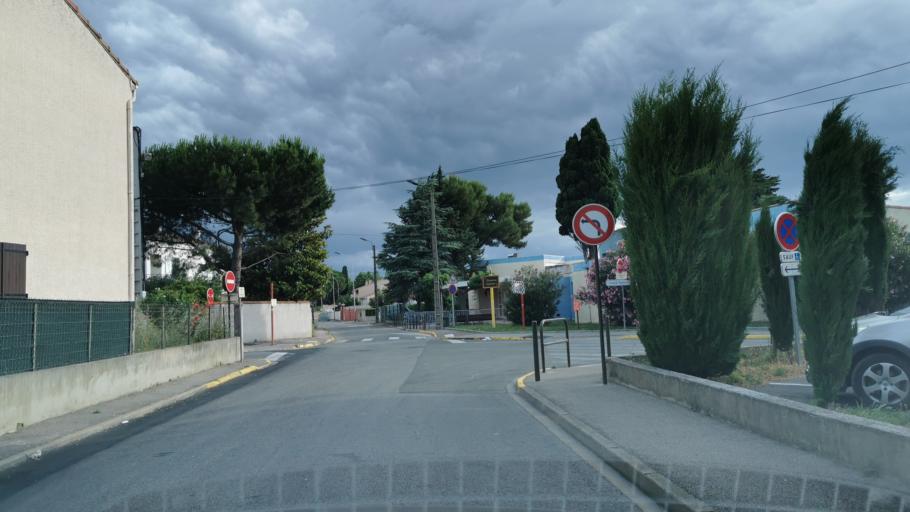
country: FR
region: Languedoc-Roussillon
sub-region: Departement de l'Aude
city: Narbonne
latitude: 43.1955
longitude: 3.0150
